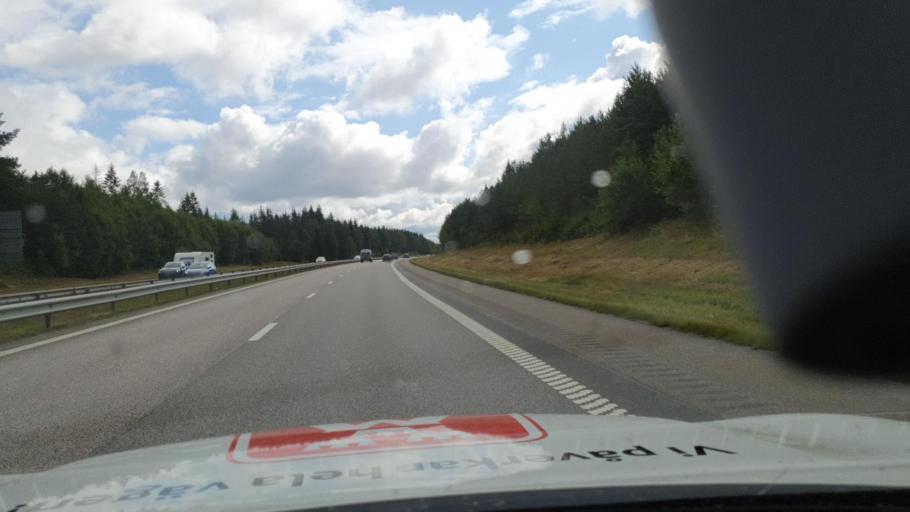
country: SE
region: Vaestra Goetaland
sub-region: Bollebygds Kommun
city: Bollebygd
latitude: 57.6714
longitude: 12.6256
